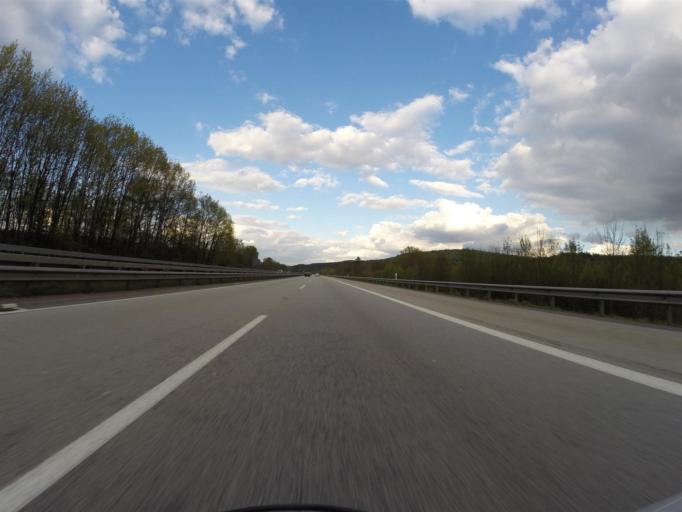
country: DE
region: Rheinland-Pfalz
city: Bechhofen
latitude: 49.3731
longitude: 7.3904
